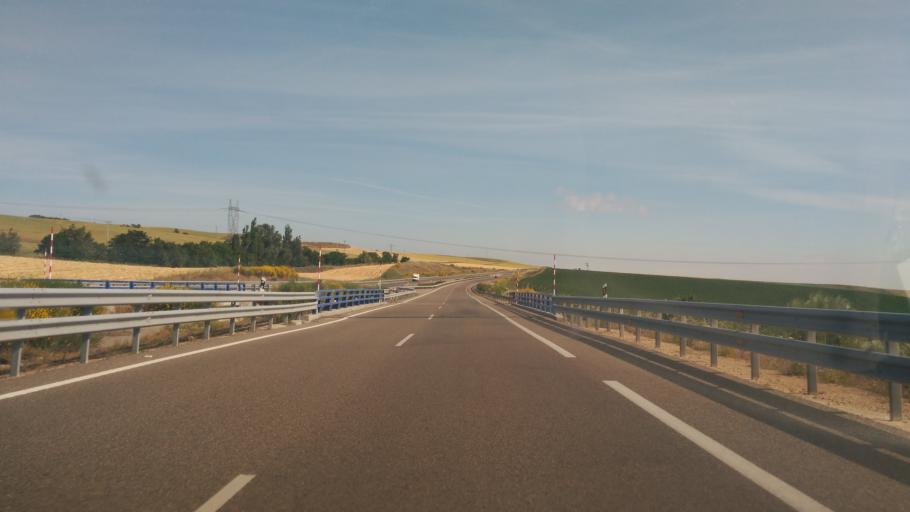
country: ES
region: Castille and Leon
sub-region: Provincia de Zamora
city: Cazurra
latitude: 41.3928
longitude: -5.7170
